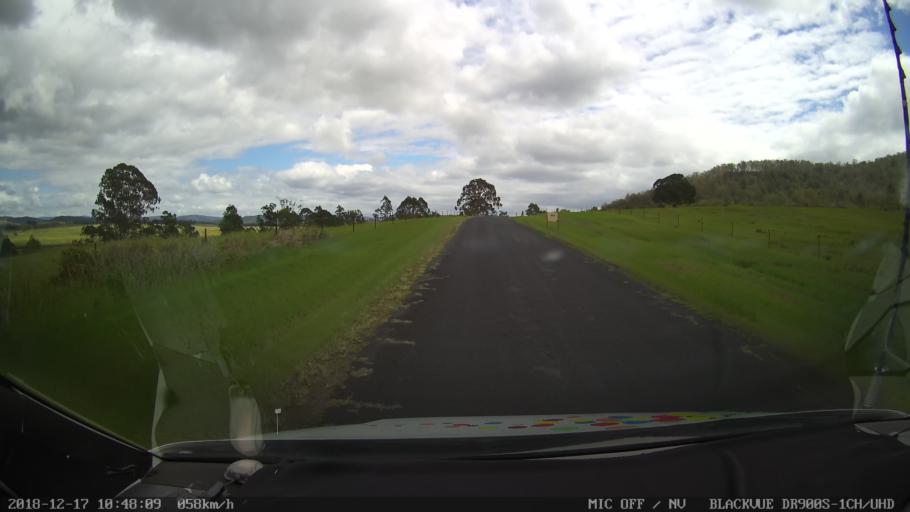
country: AU
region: New South Wales
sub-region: Clarence Valley
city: Gordon
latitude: -28.8751
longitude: 152.5706
